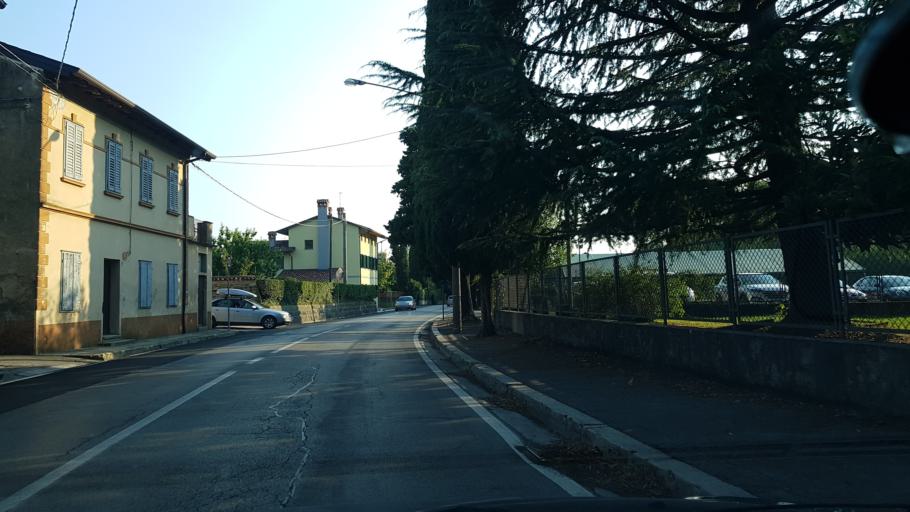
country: IT
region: Friuli Venezia Giulia
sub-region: Provincia di Gorizia
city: Gorizia
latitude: 45.9620
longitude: 13.6150
